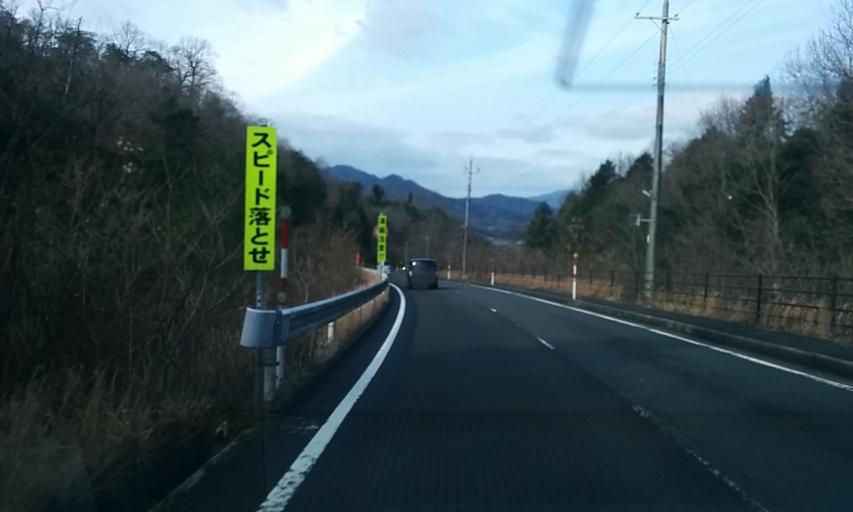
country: JP
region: Kyoto
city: Miyazu
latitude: 35.5832
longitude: 135.1141
